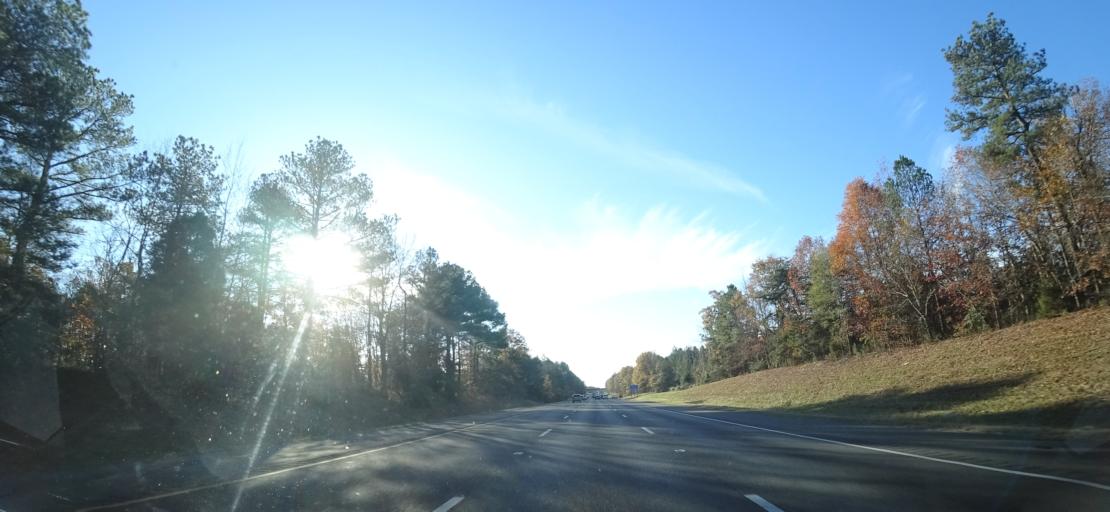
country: US
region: Virginia
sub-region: Caroline County
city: Bowling Green
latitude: 38.0005
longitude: -77.4956
